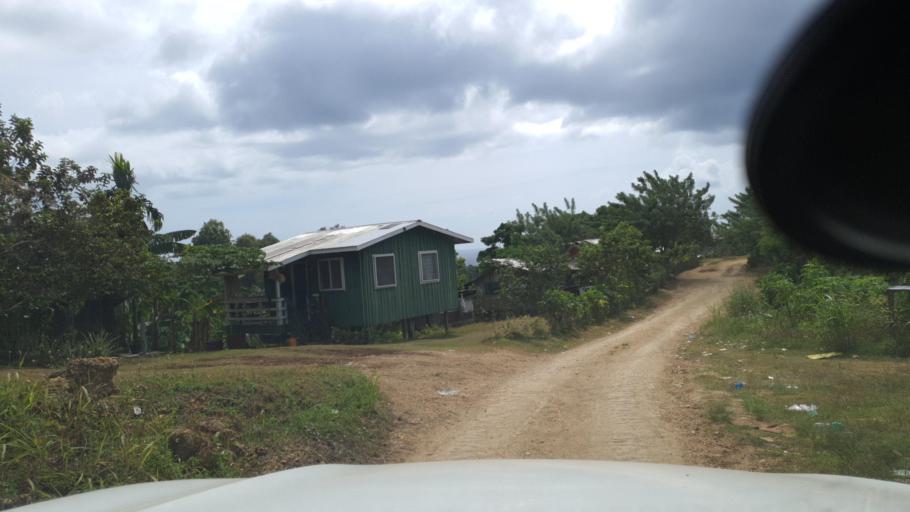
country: SB
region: Guadalcanal
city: Honiara
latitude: -9.4338
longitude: 159.9286
